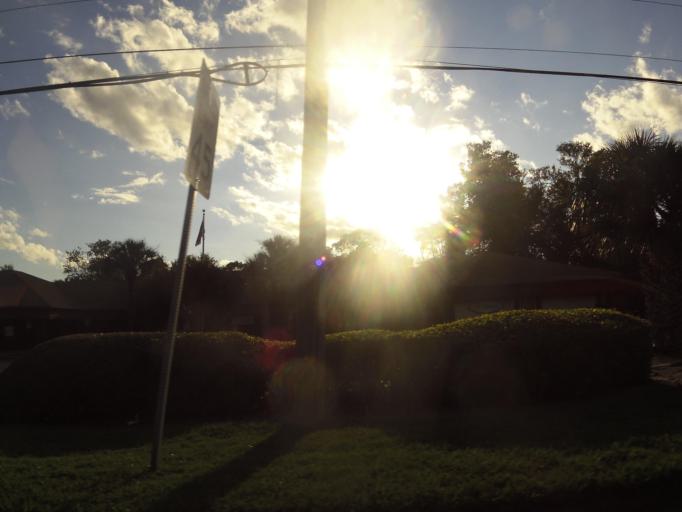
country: US
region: Florida
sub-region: Nassau County
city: Fernandina Beach
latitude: 30.6522
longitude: -81.4543
